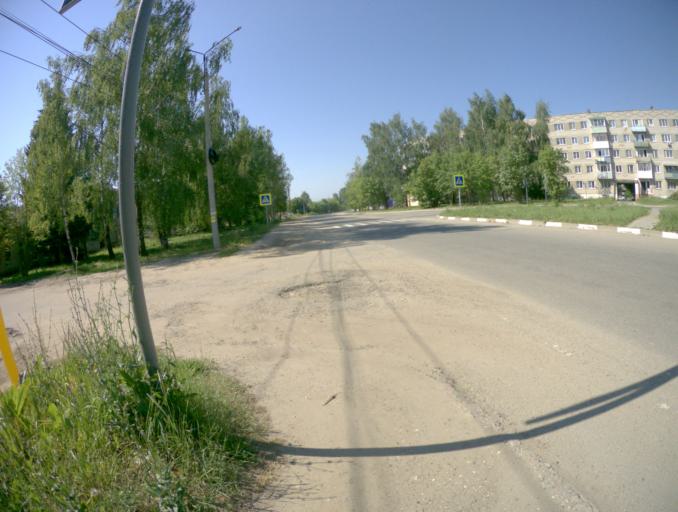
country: RU
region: Vladimir
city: Novovyazniki
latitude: 56.2310
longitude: 42.1982
